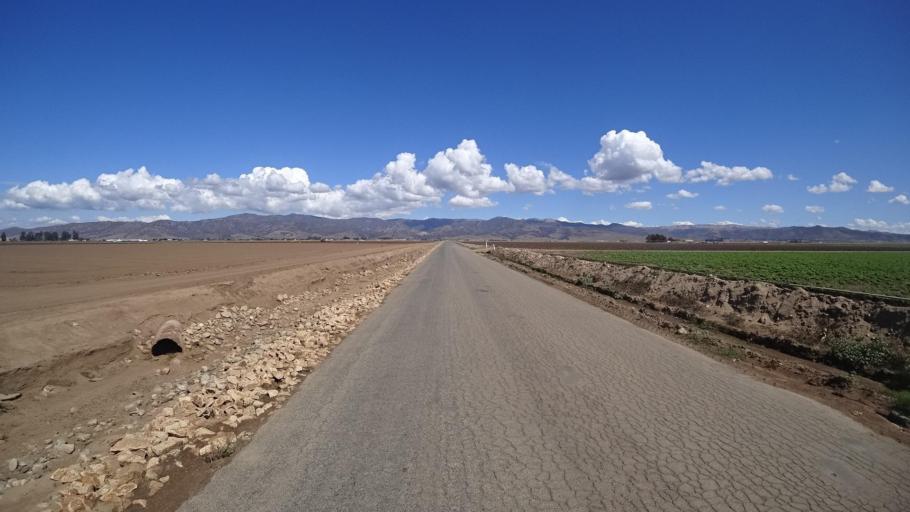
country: US
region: California
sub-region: Monterey County
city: Chualar
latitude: 36.5972
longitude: -121.5215
